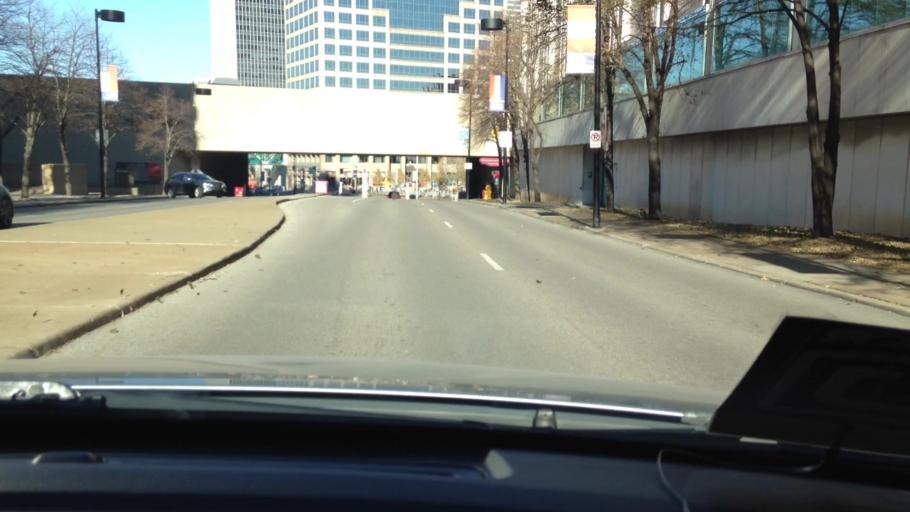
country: US
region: Missouri
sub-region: Jackson County
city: Kansas City
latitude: 39.0811
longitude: -94.5825
